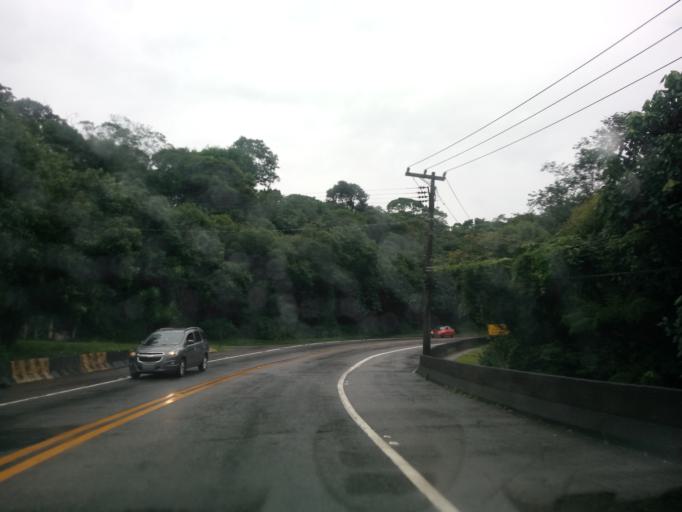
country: BR
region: Sao Paulo
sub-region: Sao Bernardo Do Campo
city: Sao Bernardo do Campo
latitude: -23.7860
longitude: -46.5079
